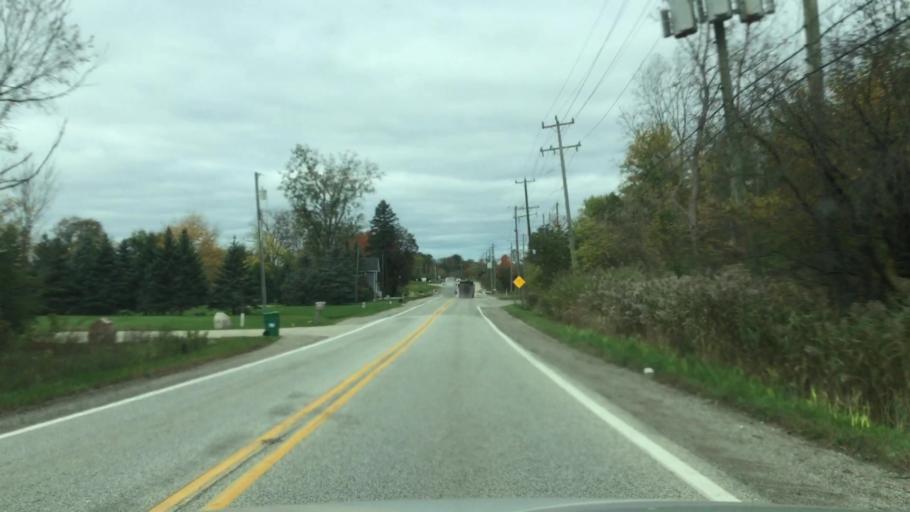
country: US
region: Michigan
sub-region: Macomb County
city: Romeo
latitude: 42.8052
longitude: -82.9651
